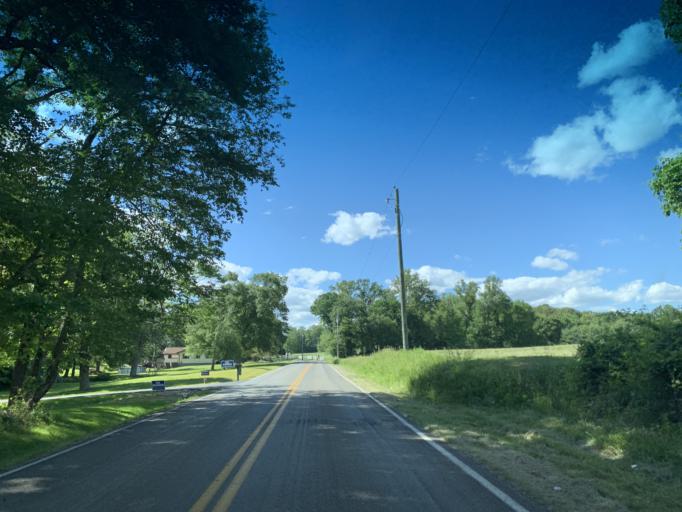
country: US
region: Maryland
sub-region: Cecil County
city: North East
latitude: 39.5467
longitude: -75.9191
